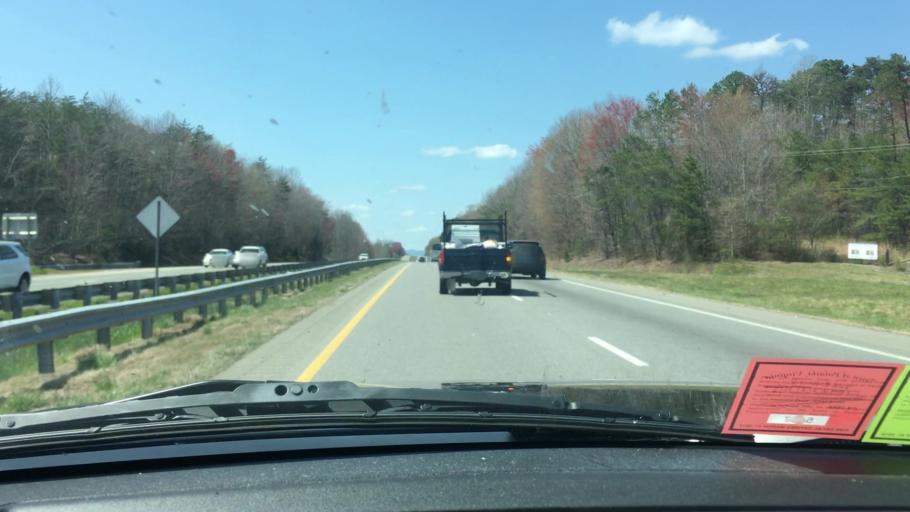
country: US
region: North Carolina
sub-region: Surry County
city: Pilot Mountain
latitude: 36.4096
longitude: -80.5007
